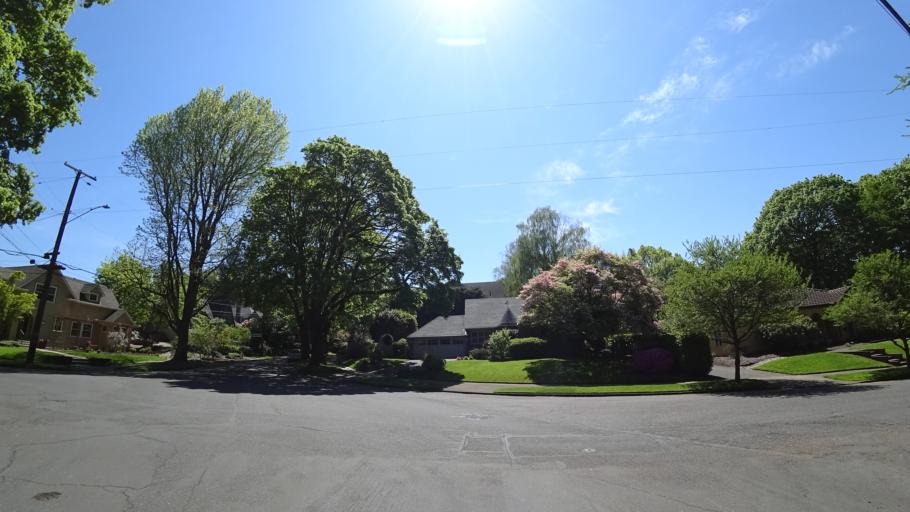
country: US
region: Oregon
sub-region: Clackamas County
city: Milwaukie
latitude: 45.4747
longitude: -122.6266
